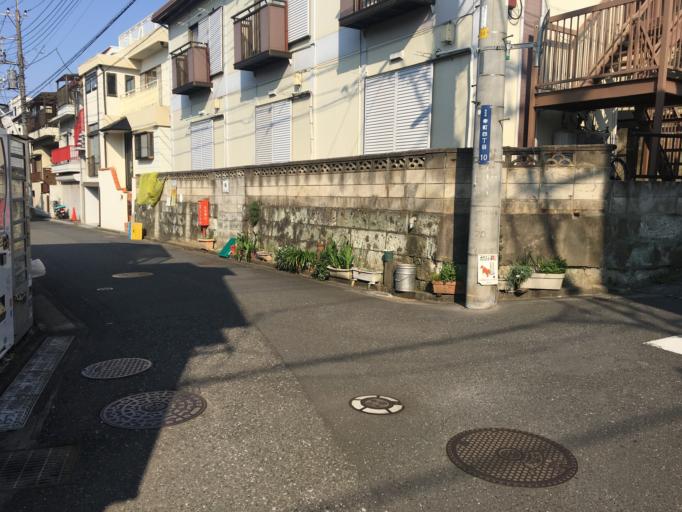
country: JP
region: Saitama
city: Shiki
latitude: 35.8226
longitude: 139.5619
